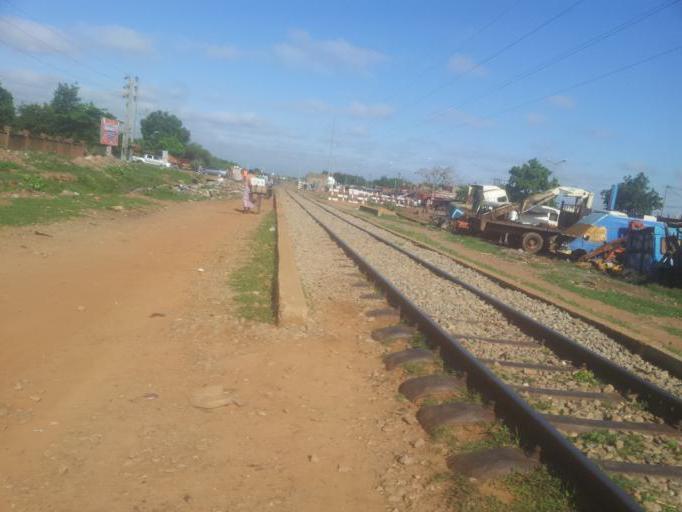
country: BF
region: Centre
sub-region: Kadiogo Province
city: Ouagadougou
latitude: 12.3701
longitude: -1.5576
